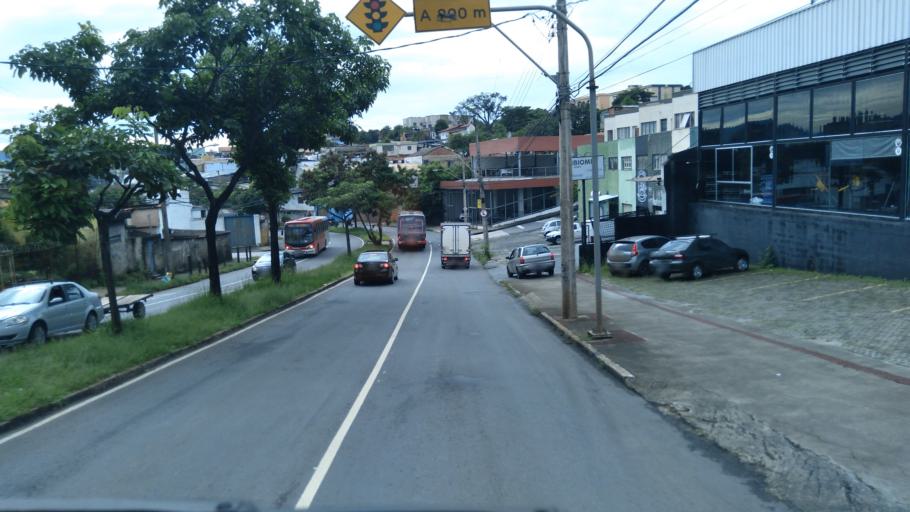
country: BR
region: Minas Gerais
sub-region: Contagem
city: Contagem
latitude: -19.9251
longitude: -44.0027
